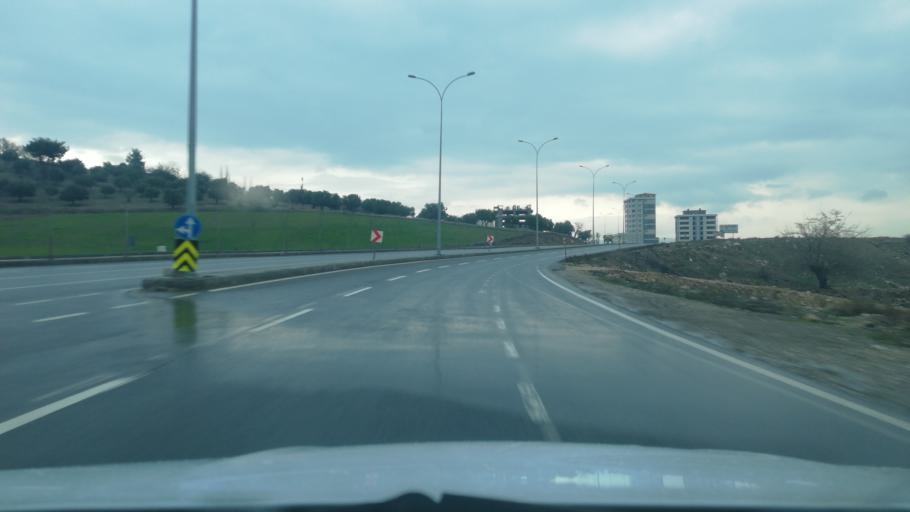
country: TR
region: Kahramanmaras
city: Kahramanmaras
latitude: 37.5817
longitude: 36.9907
